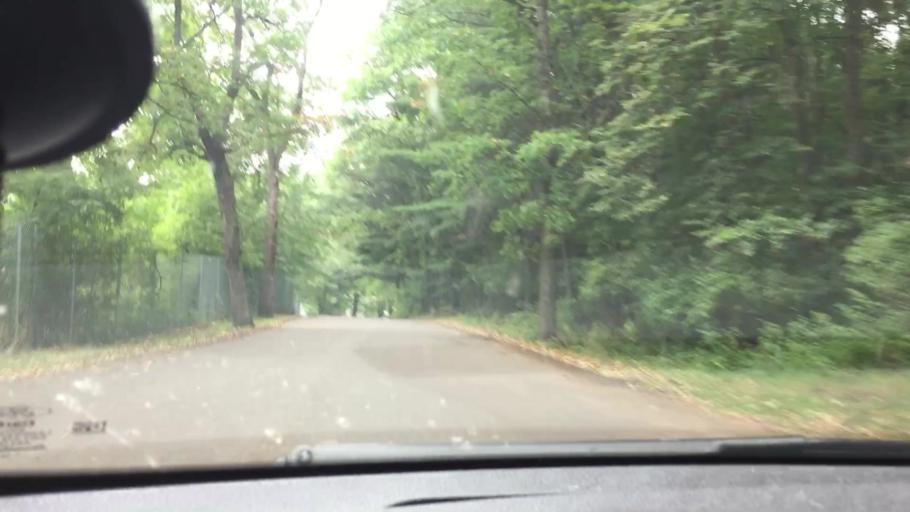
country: US
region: Wisconsin
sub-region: Chippewa County
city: Chippewa Falls
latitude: 44.9512
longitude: -91.4000
